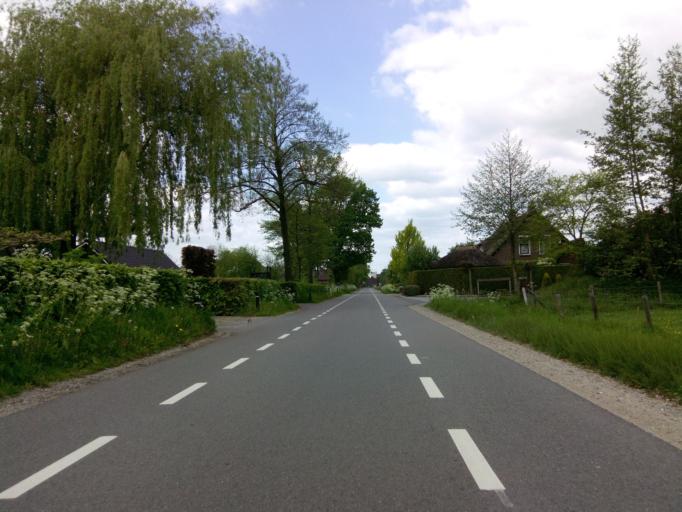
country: NL
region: Gelderland
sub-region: Gemeente Ede
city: Ederveen
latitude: 52.0601
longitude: 5.5980
